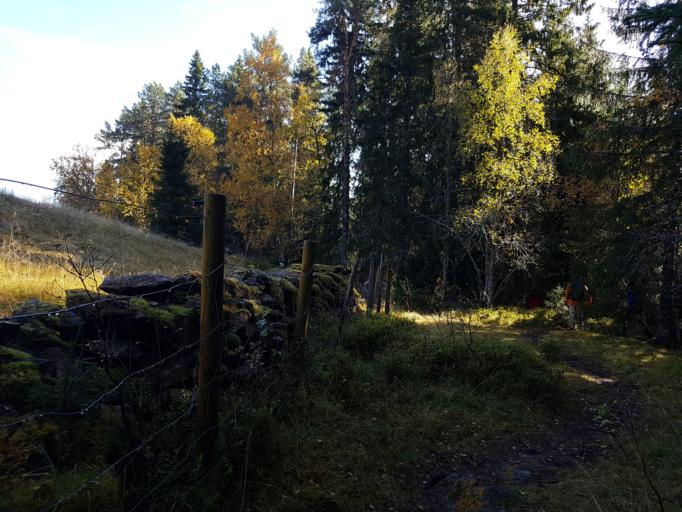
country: NO
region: Sor-Trondelag
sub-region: Trondheim
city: Trondheim
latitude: 63.4226
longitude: 10.2955
